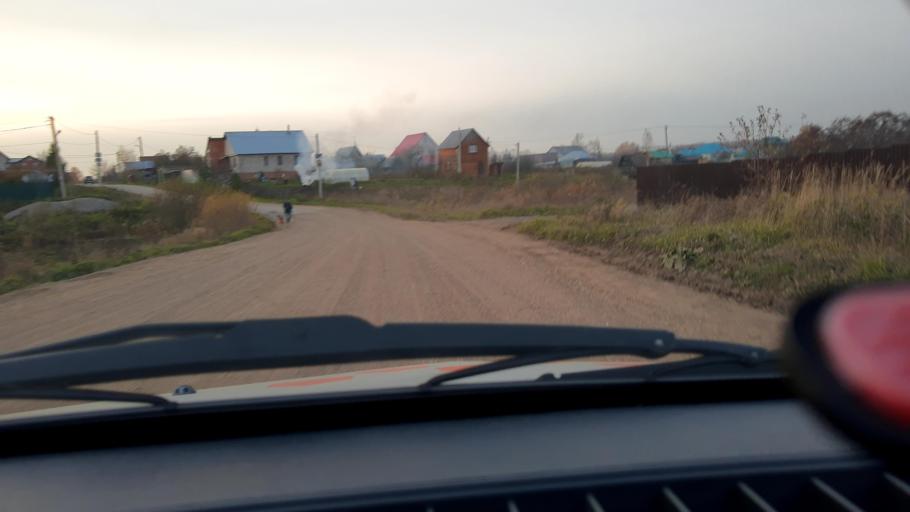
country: RU
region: Bashkortostan
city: Iglino
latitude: 54.7921
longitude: 56.3253
